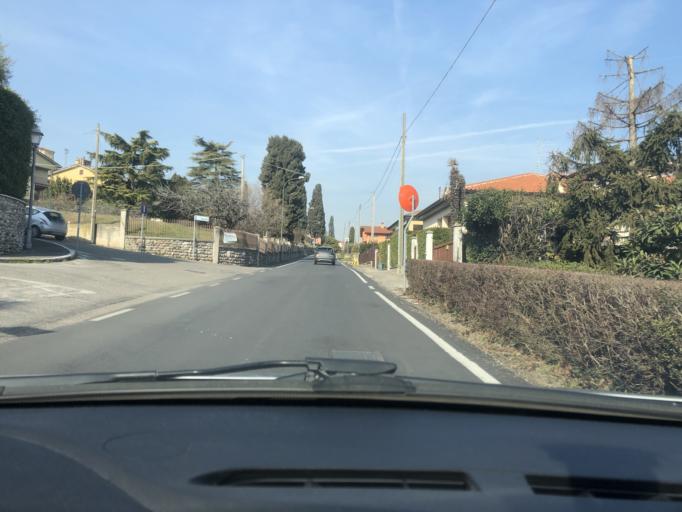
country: IT
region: Veneto
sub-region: Provincia di Verona
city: Sona
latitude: 45.4513
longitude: 10.8231
